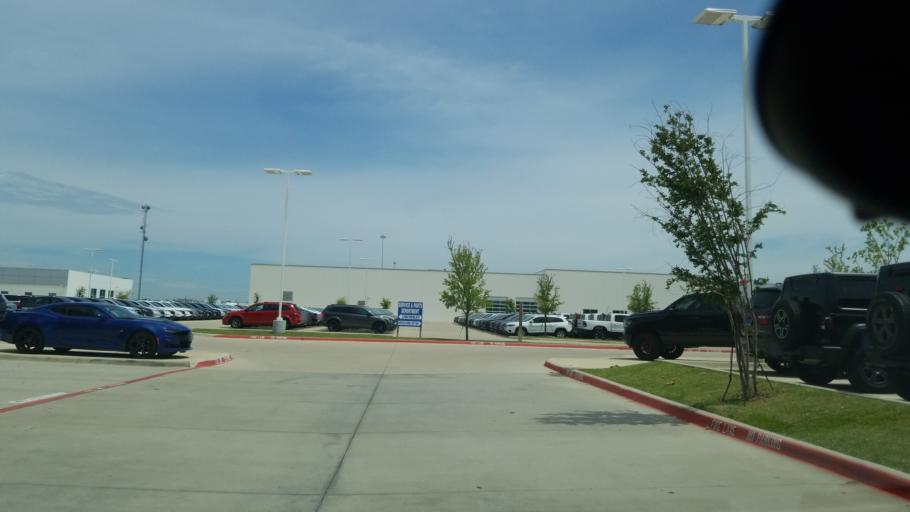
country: US
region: Texas
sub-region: Dallas County
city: Irving
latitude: 32.8389
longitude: -96.9314
